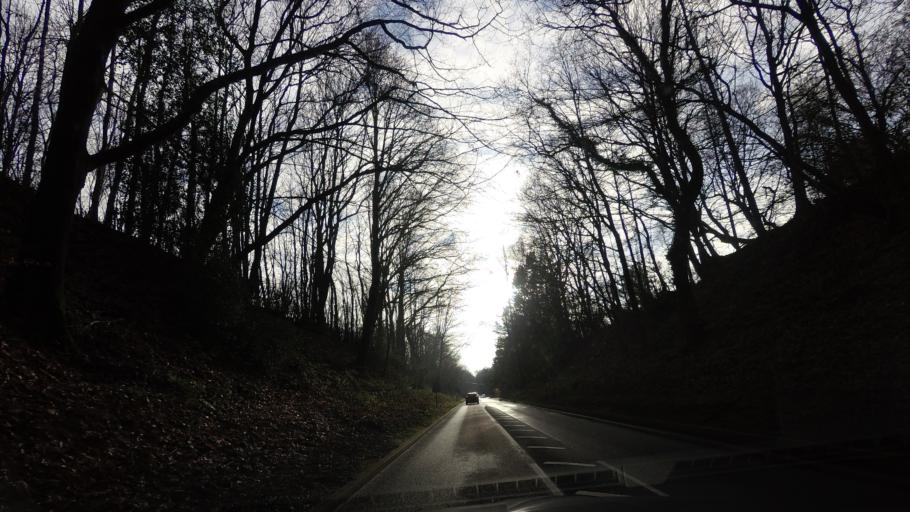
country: GB
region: England
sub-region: East Sussex
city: Battle
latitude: 50.9496
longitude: 0.4834
